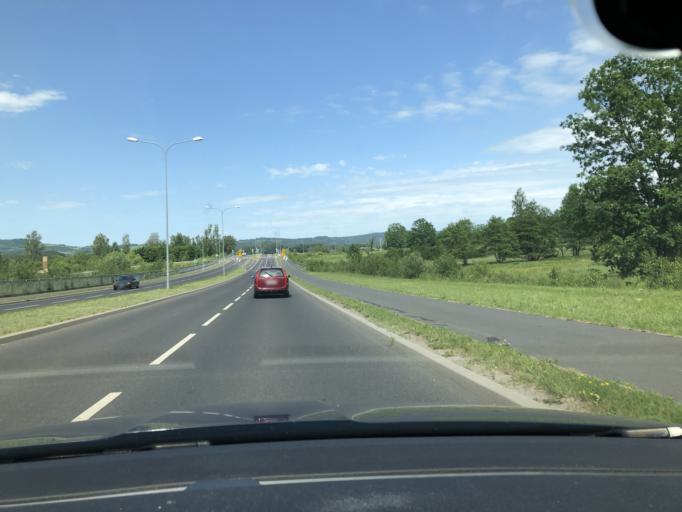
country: PL
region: Lower Silesian Voivodeship
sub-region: Jelenia Gora
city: Jelenia Gora
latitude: 50.8962
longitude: 15.7693
